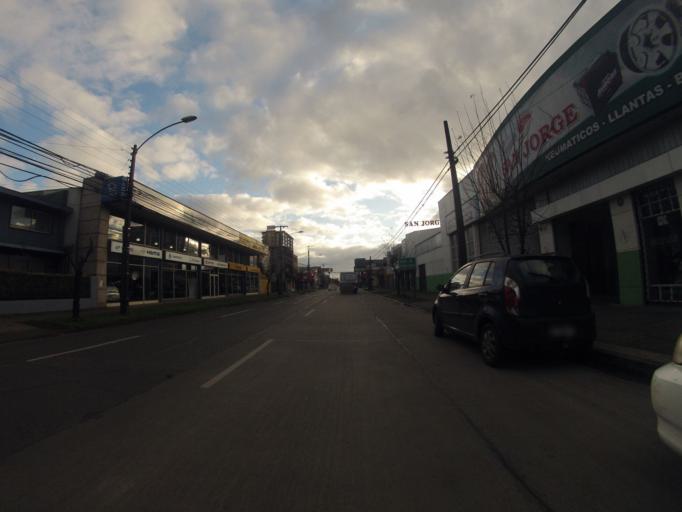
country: CL
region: Araucania
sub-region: Provincia de Cautin
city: Temuco
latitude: -38.7422
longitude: -72.5932
